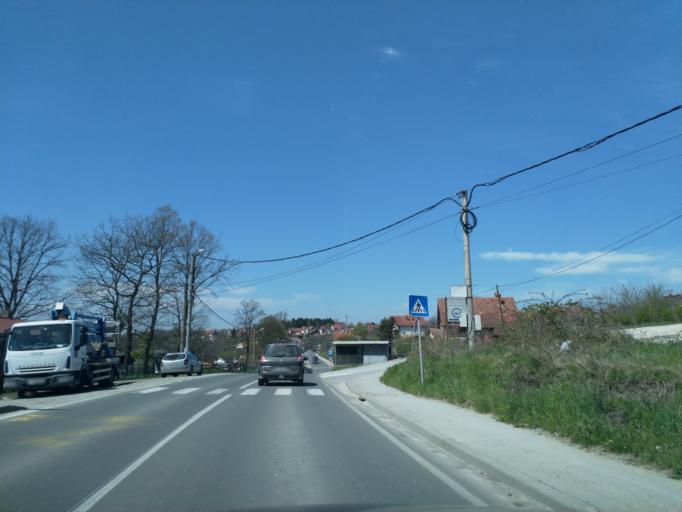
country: RS
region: Central Serbia
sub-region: Sumadijski Okrug
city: Arangelovac
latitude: 44.3265
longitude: 20.5244
